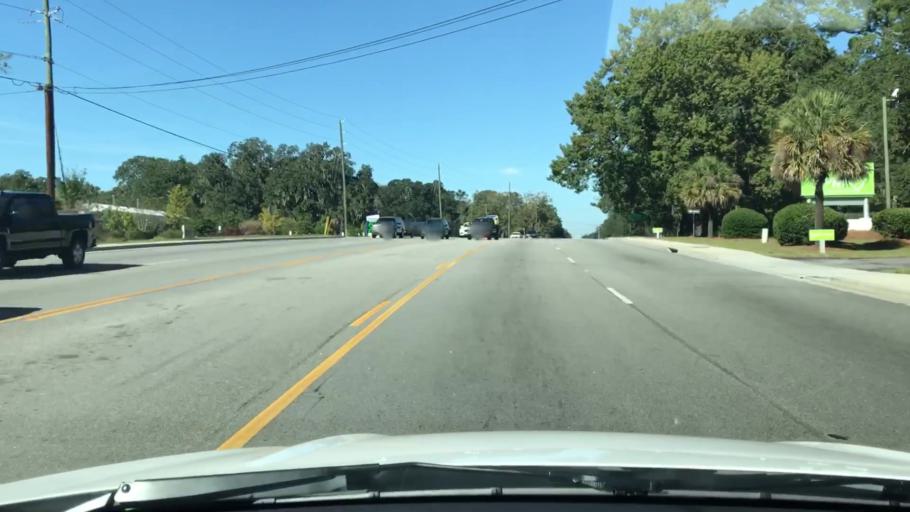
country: US
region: South Carolina
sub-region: Beaufort County
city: Burton
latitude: 32.4519
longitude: -80.7321
